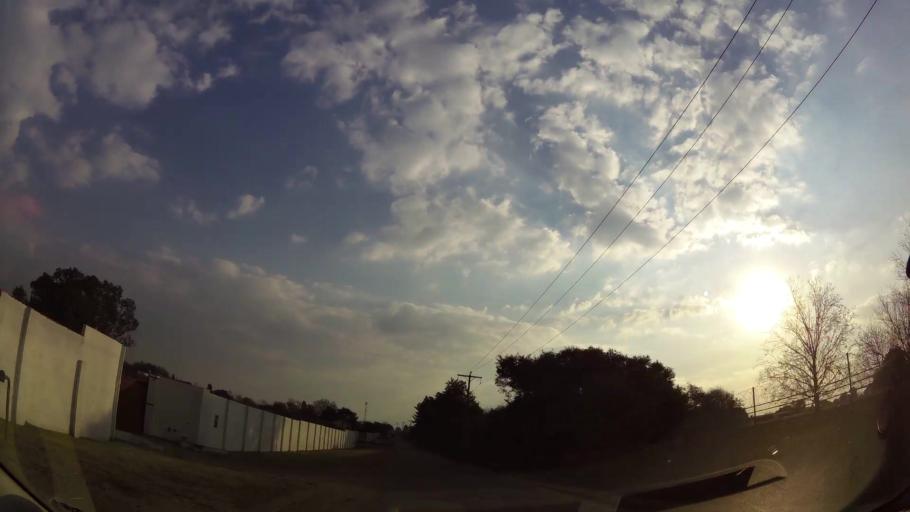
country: ZA
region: Gauteng
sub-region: Ekurhuleni Metropolitan Municipality
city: Benoni
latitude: -26.1204
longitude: 28.2973
